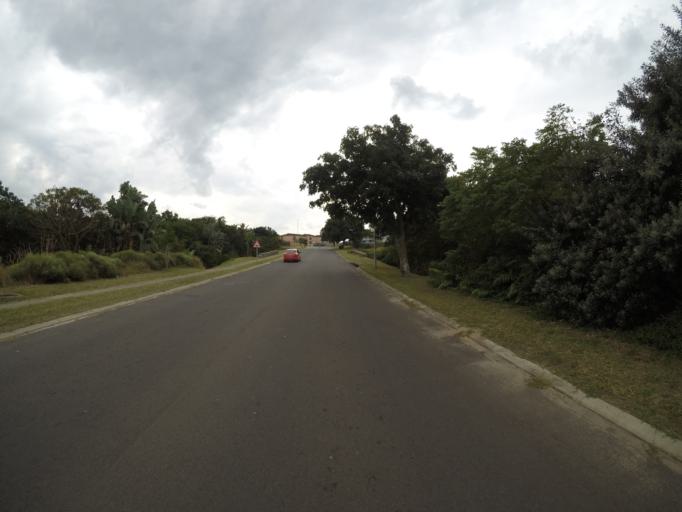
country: ZA
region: KwaZulu-Natal
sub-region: uThungulu District Municipality
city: Richards Bay
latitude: -28.7333
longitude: 32.0503
